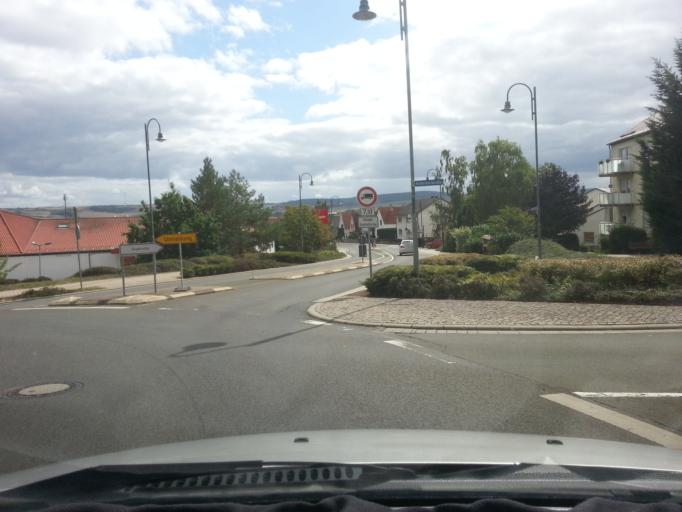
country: DE
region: Rheinland-Pfalz
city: Eisenberg
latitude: 49.5640
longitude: 8.0628
